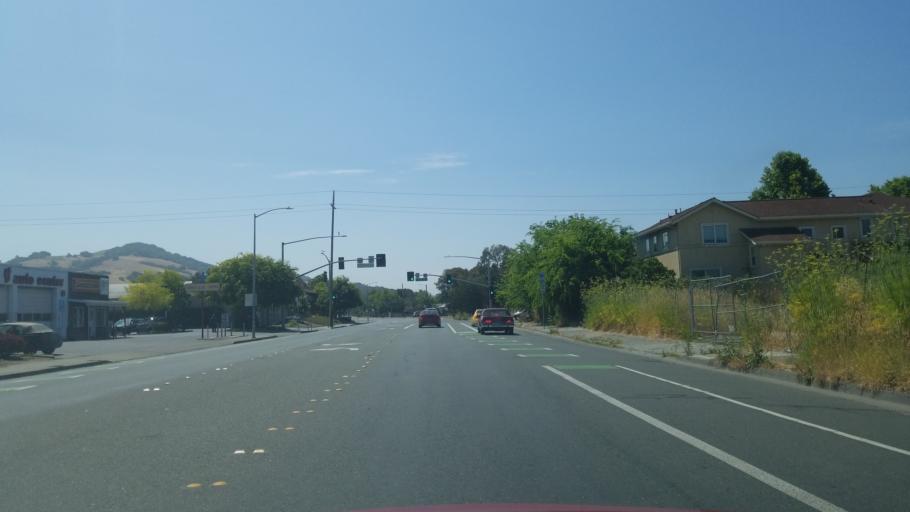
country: US
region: California
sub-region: Sonoma County
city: Santa Rosa
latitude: 38.4237
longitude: -122.7081
